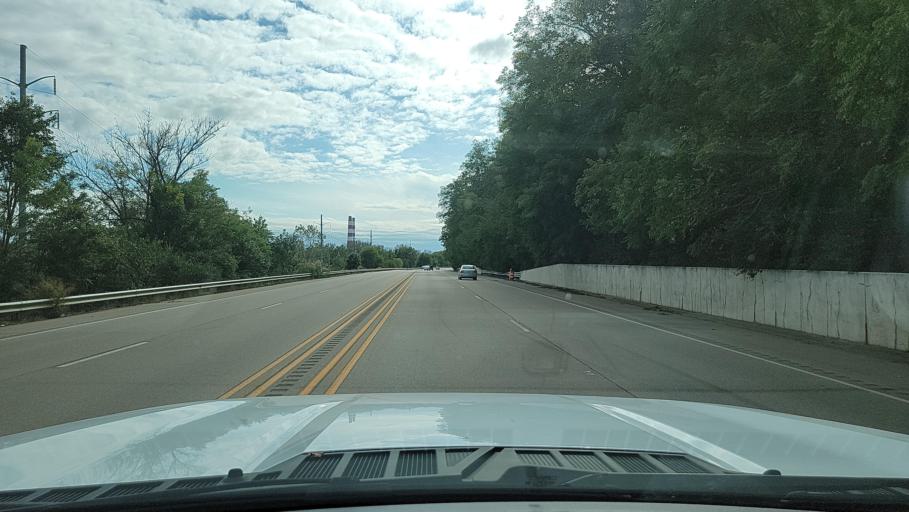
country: US
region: Illinois
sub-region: Tazewell County
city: North Pekin
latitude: 40.6141
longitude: -89.6587
